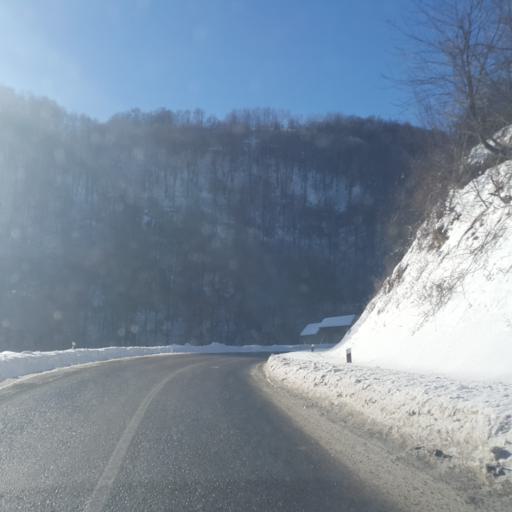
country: RS
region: Central Serbia
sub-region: Rasinski Okrug
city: Aleksandrovac
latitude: 43.3062
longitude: 20.9042
